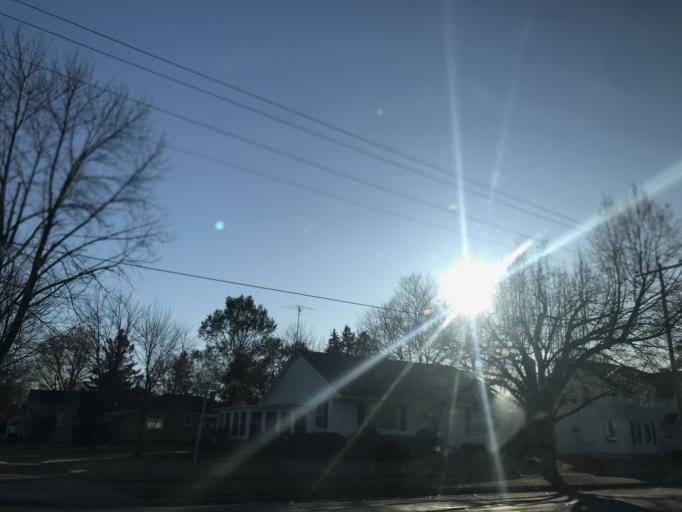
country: US
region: Wisconsin
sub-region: Marinette County
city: Peshtigo
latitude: 45.0550
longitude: -87.7420
